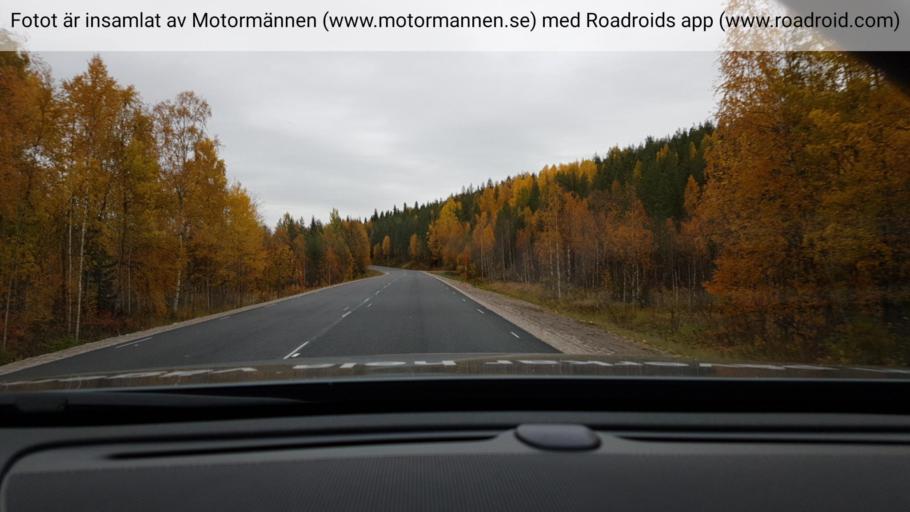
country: SE
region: Norrbotten
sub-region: Overkalix Kommun
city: OEverkalix
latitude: 66.4601
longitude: 22.7915
